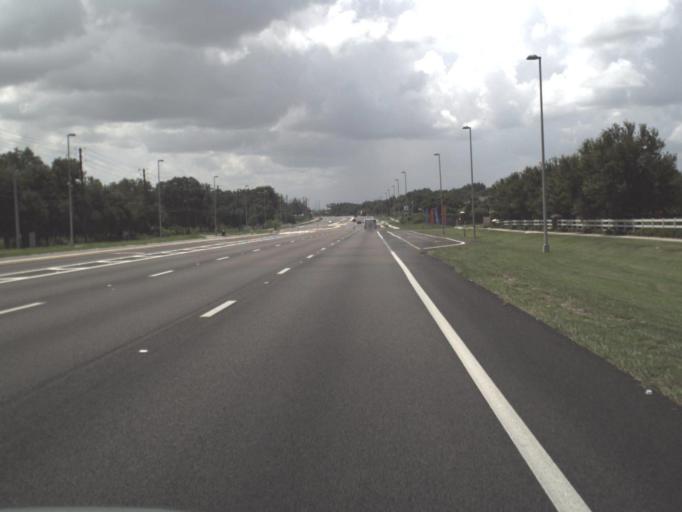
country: US
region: Florida
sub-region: Hillsborough County
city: Riverview
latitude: 27.8074
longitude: -82.3338
